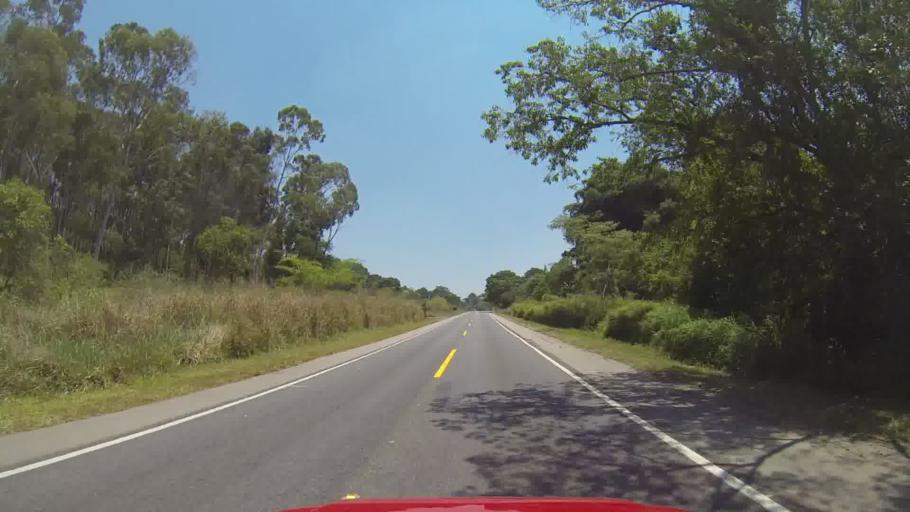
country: BR
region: Minas Gerais
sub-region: Itapecerica
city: Itapecerica
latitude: -20.2949
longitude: -45.1653
